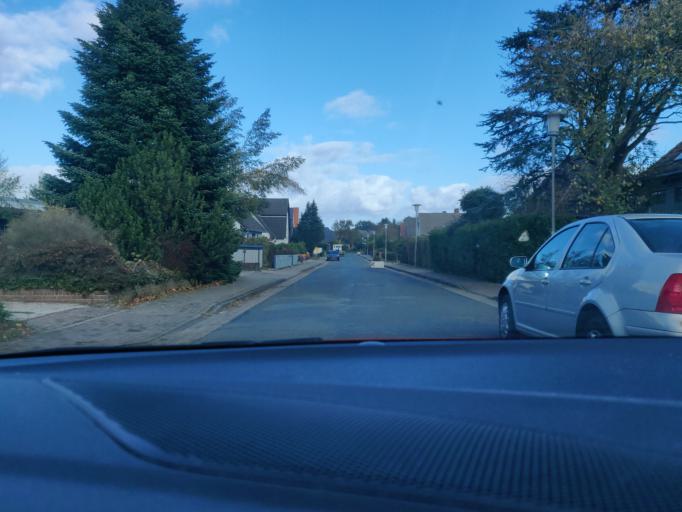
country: DE
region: Lower Saxony
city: Cuxhaven
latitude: 53.8712
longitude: 8.6481
